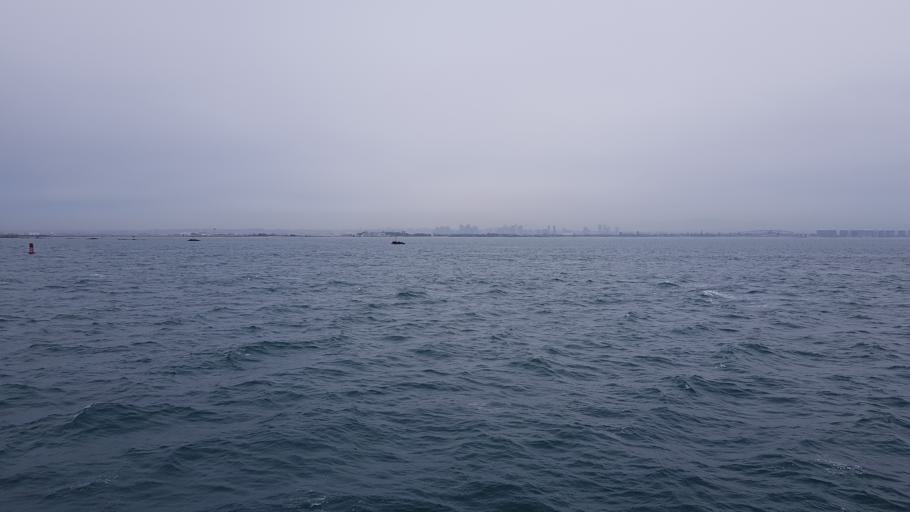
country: US
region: California
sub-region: San Diego County
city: Coronado
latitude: 32.6624
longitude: -117.2271
